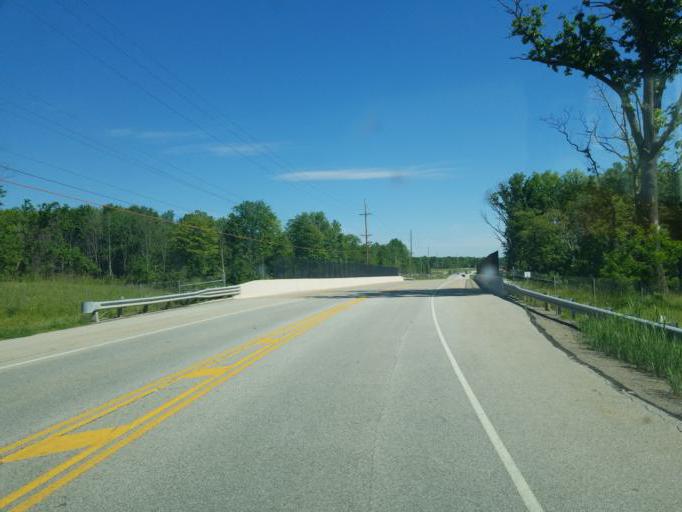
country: US
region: Ohio
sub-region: Summit County
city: Boston Heights
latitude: 41.2577
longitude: -81.5043
